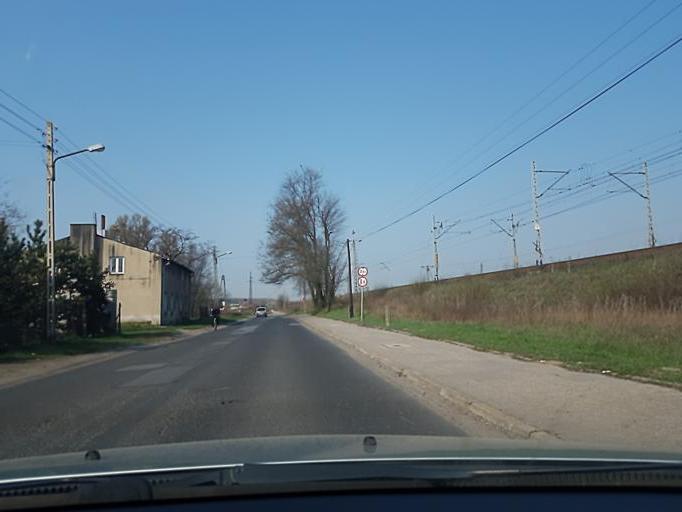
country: PL
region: Lodz Voivodeship
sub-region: Powiat kutnowski
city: Kutno
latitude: 52.2221
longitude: 19.3822
